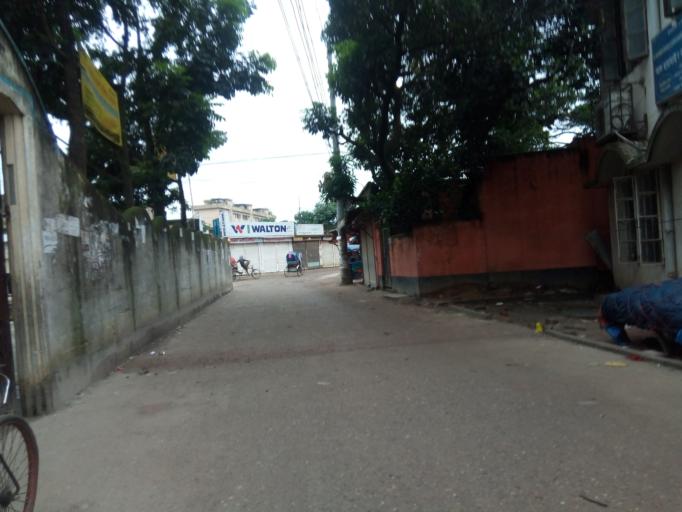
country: BD
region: Dhaka
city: Tungi
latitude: 23.8461
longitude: 90.4202
